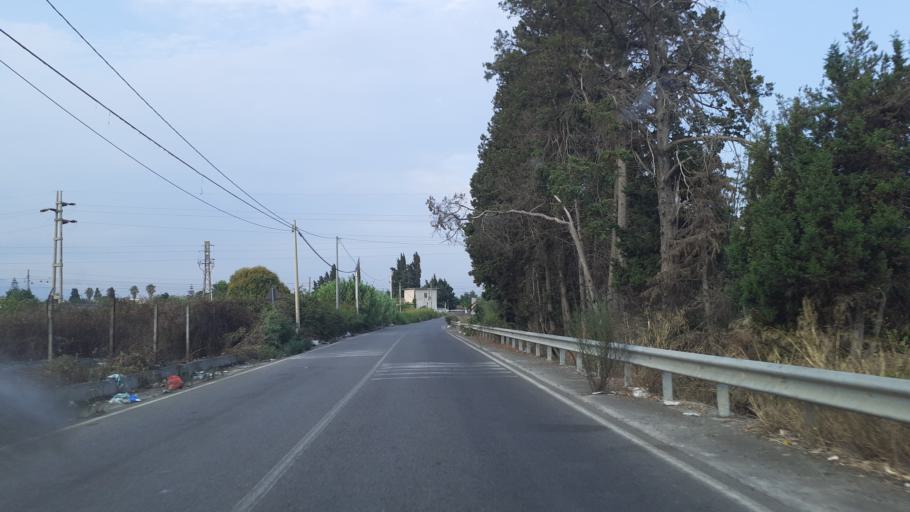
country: IT
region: Sicily
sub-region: Catania
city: Catania
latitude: 37.4545
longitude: 15.0279
